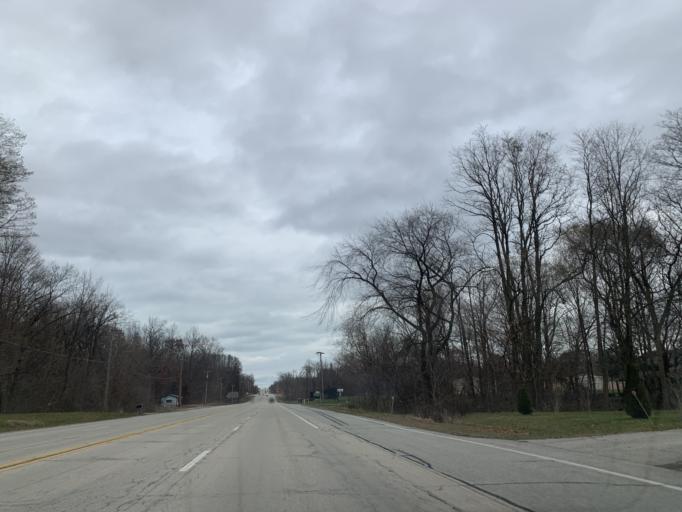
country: US
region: Indiana
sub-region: LaPorte County
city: Trail Creek
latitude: 41.7048
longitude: -86.8259
